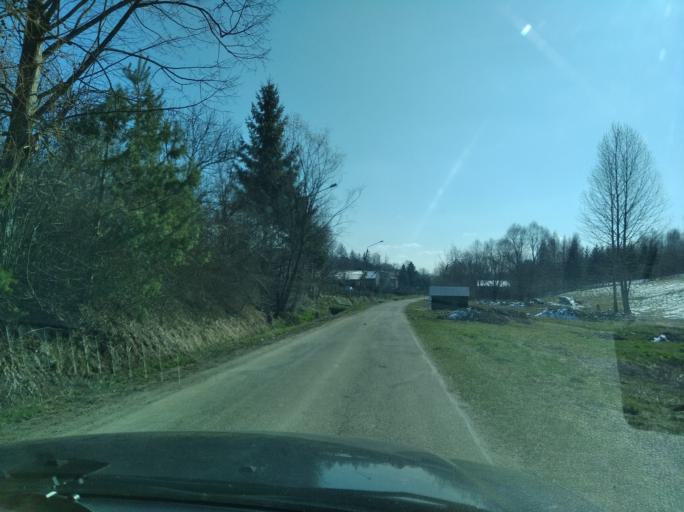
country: PL
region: Subcarpathian Voivodeship
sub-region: Powiat strzyzowski
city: Gwoznica Gorna
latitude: 49.8177
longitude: 22.0219
